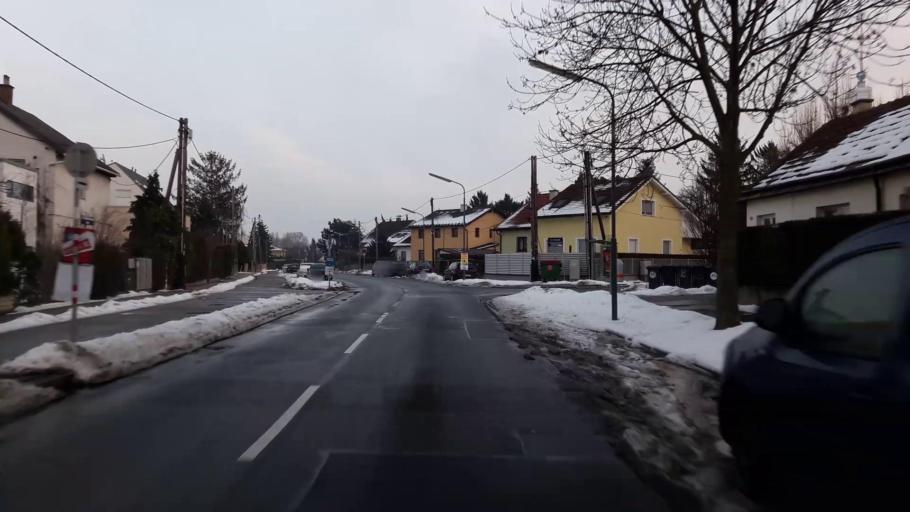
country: AT
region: Vienna
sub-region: Wien Stadt
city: Vienna
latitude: 48.2468
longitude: 16.4042
